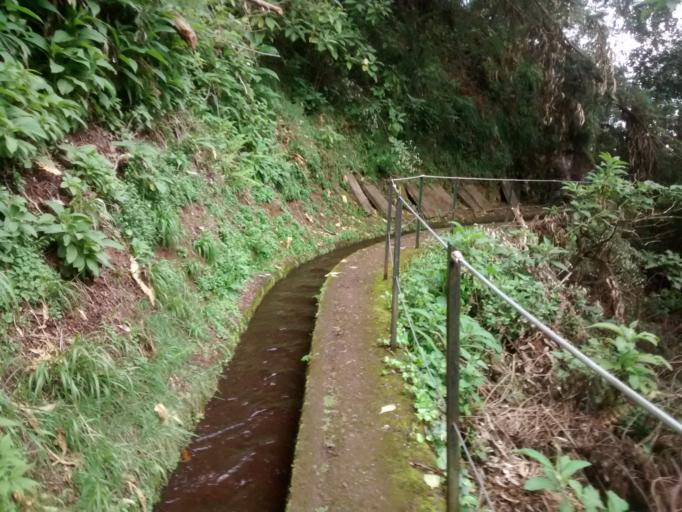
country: PT
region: Madeira
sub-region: Santana
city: Santana
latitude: 32.8112
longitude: -16.9308
